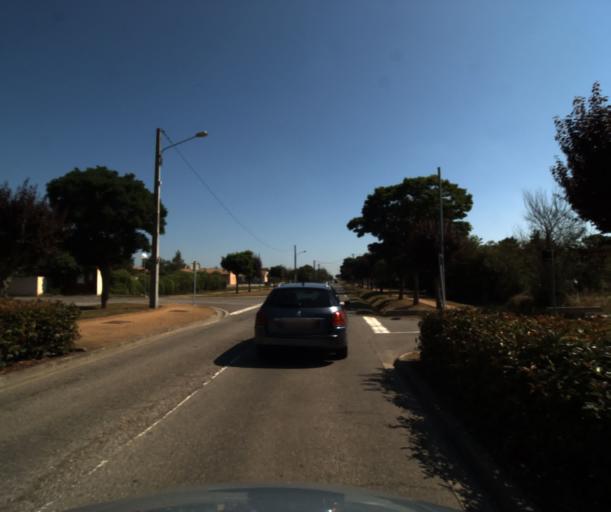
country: FR
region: Midi-Pyrenees
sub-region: Departement de la Haute-Garonne
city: Labastidette
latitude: 43.4635
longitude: 1.2480
